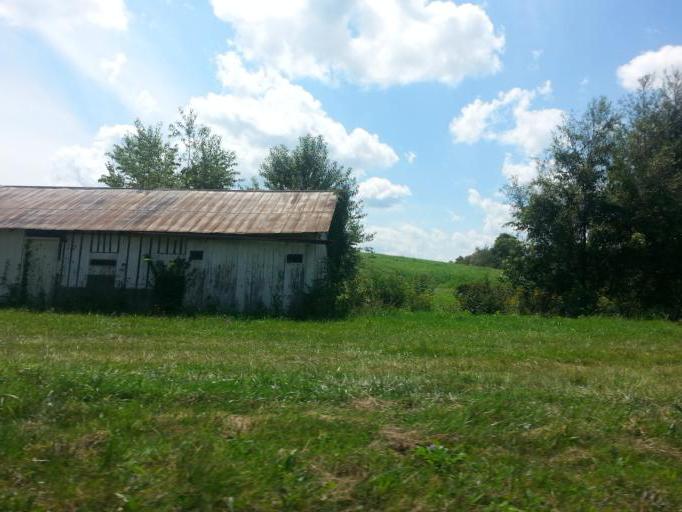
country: US
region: Virginia
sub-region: Washington County
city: Abingdon
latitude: 36.7106
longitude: -81.9261
